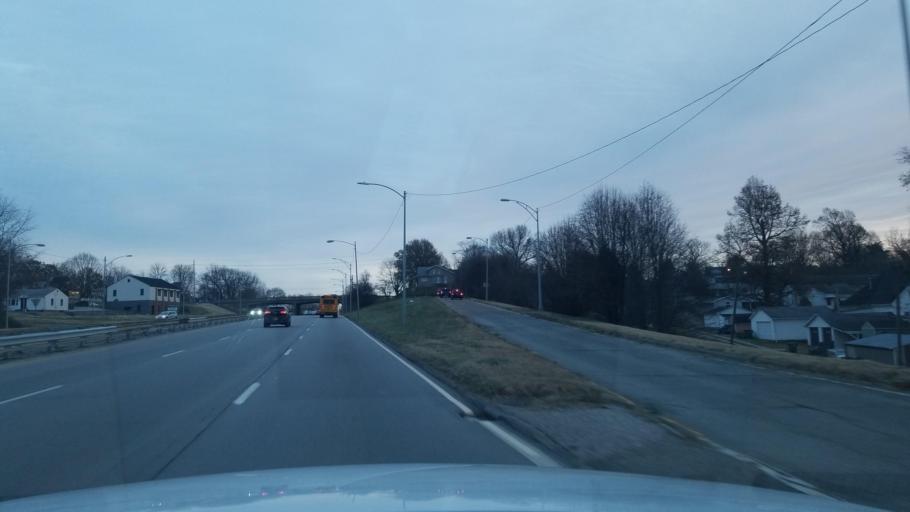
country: US
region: Indiana
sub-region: Vanderburgh County
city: Evansville
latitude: 37.9775
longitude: -87.6126
